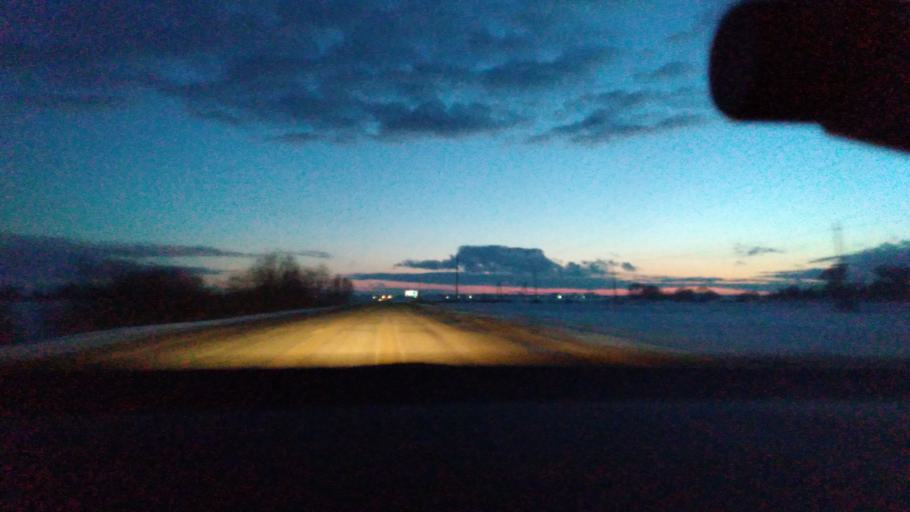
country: RU
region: Moskovskaya
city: Krasnaya Poyma
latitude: 55.0728
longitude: 39.1292
